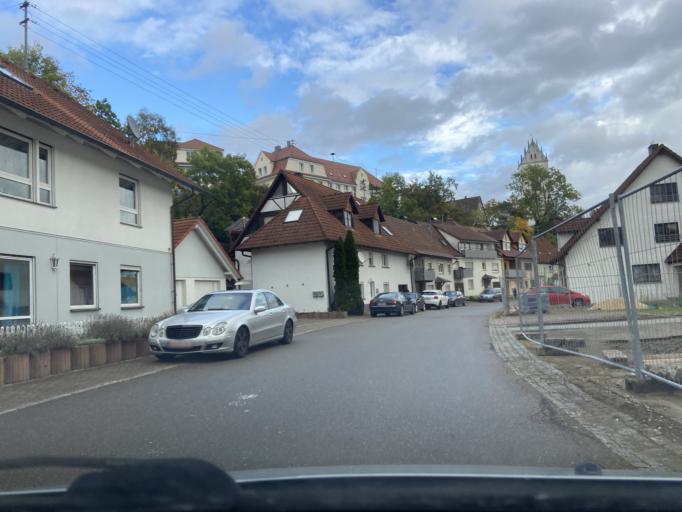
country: DE
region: Baden-Wuerttemberg
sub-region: Tuebingen Region
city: Bingen
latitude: 48.1115
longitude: 9.2742
